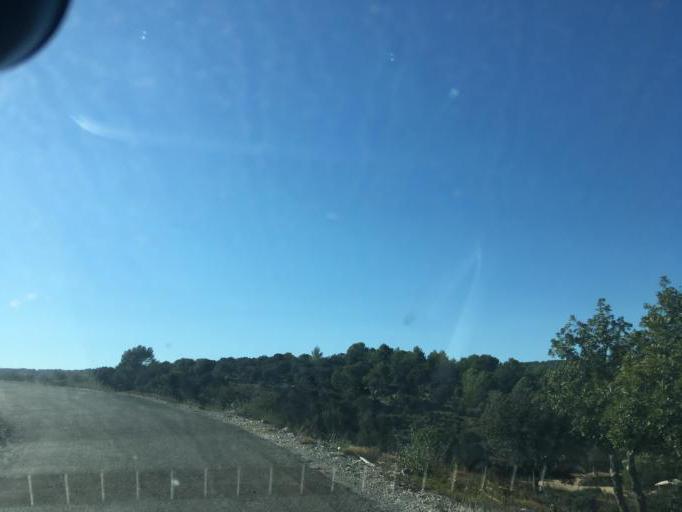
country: FR
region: Provence-Alpes-Cote d'Azur
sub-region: Departement des Alpes-de-Haute-Provence
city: Riez
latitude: 43.7442
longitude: 6.0983
